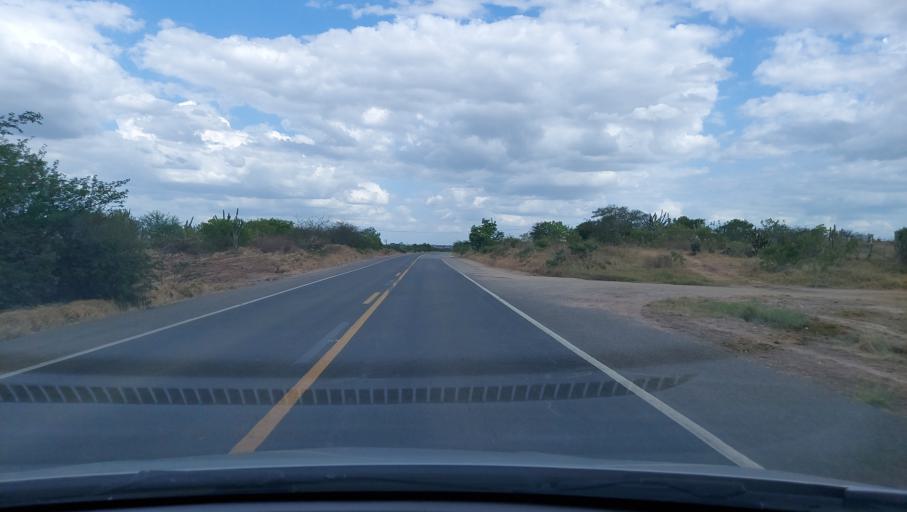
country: BR
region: Bahia
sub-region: Castro Alves
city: Castro Alves
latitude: -12.5480
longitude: -39.5544
